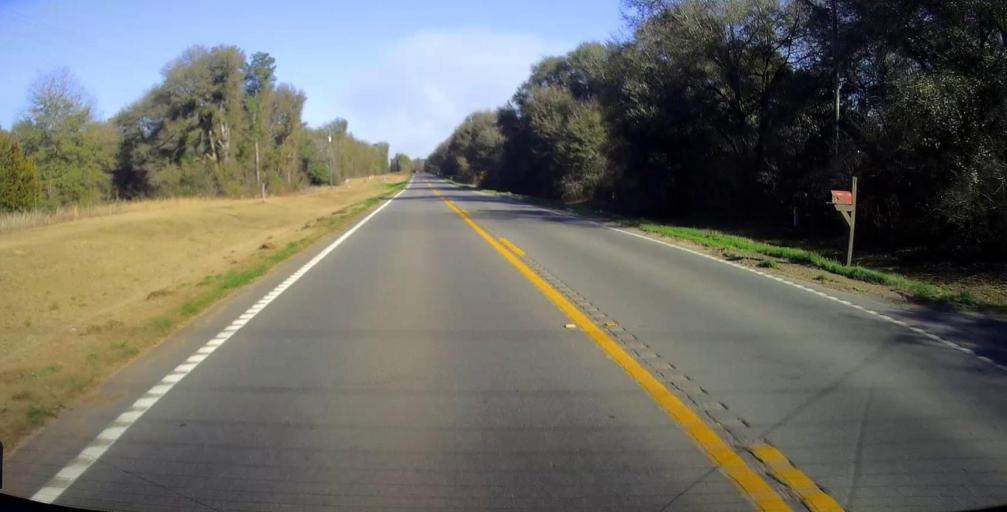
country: US
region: Georgia
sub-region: Macon County
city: Oglethorpe
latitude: 32.3319
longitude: -84.1011
